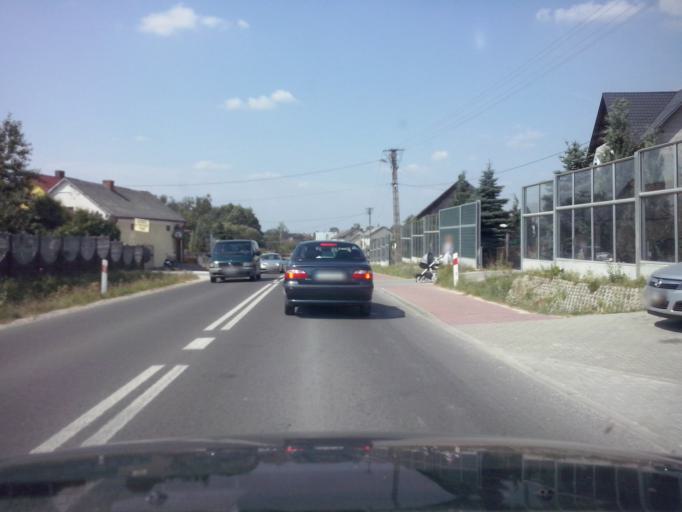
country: PL
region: Swietokrzyskie
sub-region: Powiat buski
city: Gnojno
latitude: 50.5989
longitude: 20.8657
